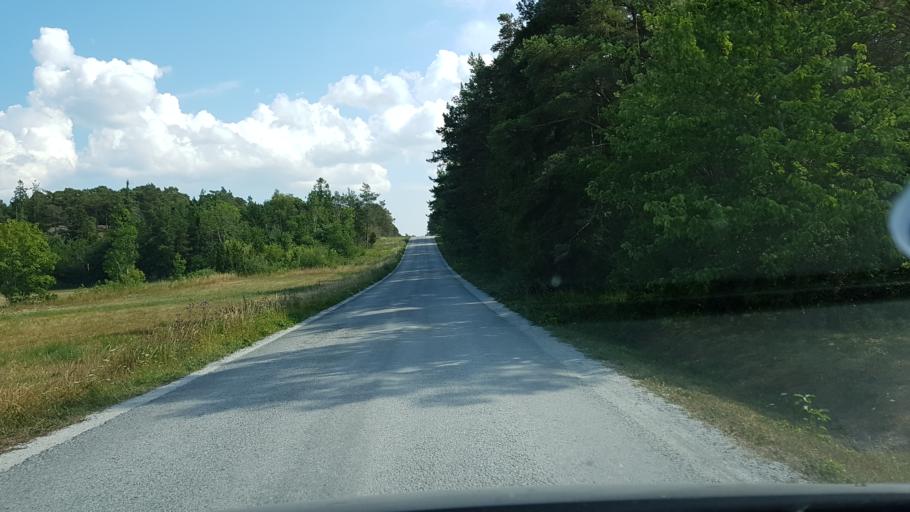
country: SE
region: Gotland
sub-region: Gotland
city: Visby
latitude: 57.8202
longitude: 18.5181
